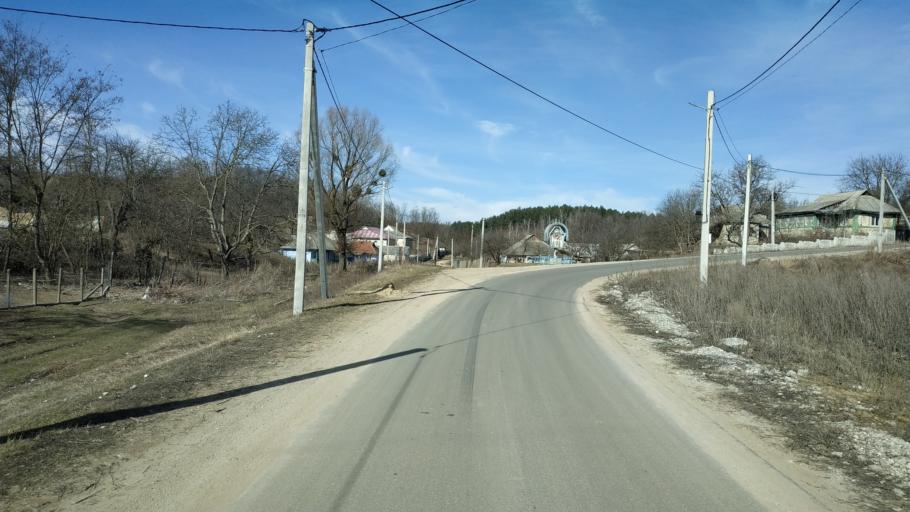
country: MD
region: Nisporeni
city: Nisporeni
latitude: 47.0981
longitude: 28.2935
